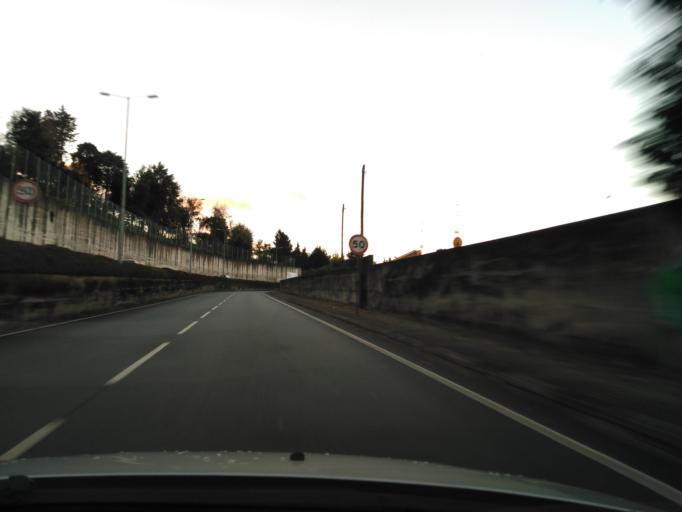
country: PT
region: Braga
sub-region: Braga
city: Braga
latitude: 41.5380
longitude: -8.4069
